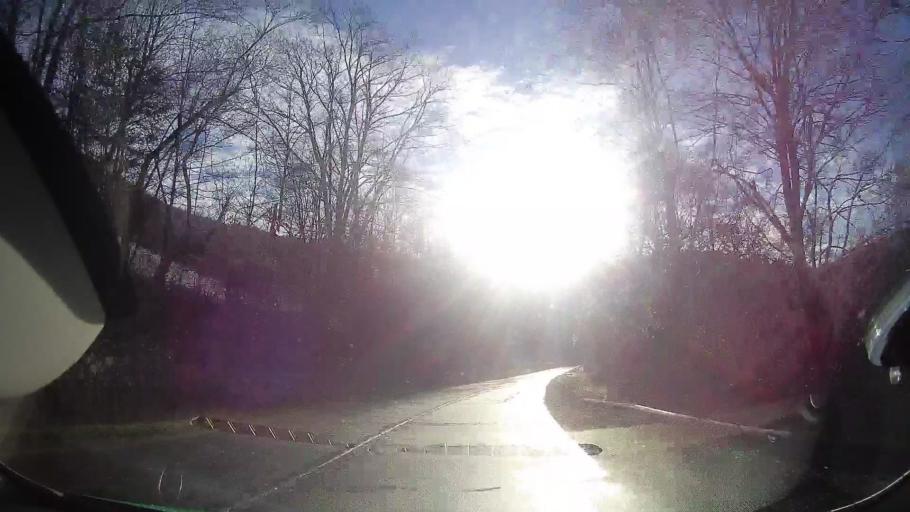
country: RO
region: Alba
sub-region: Comuna Sohodol
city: Sohodol
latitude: 46.3677
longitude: 23.0285
